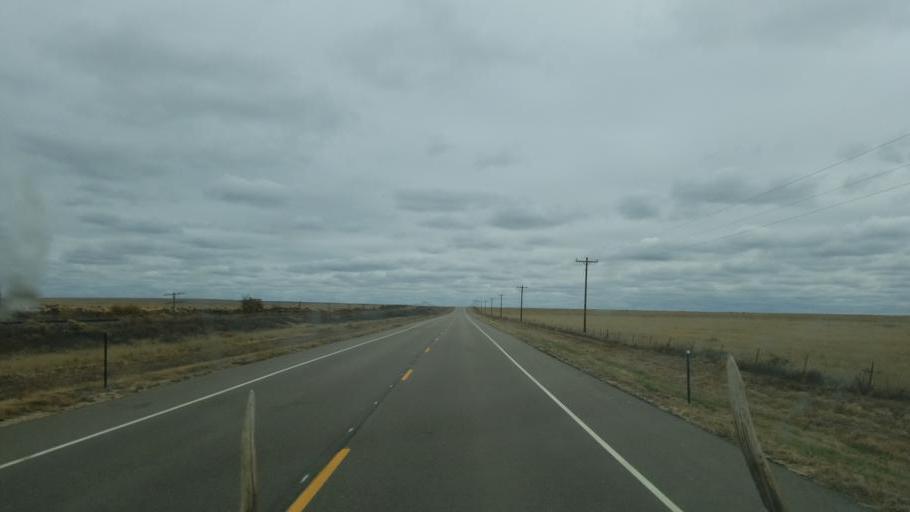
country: US
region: Colorado
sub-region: Bent County
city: Las Animas
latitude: 38.4149
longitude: -103.2782
